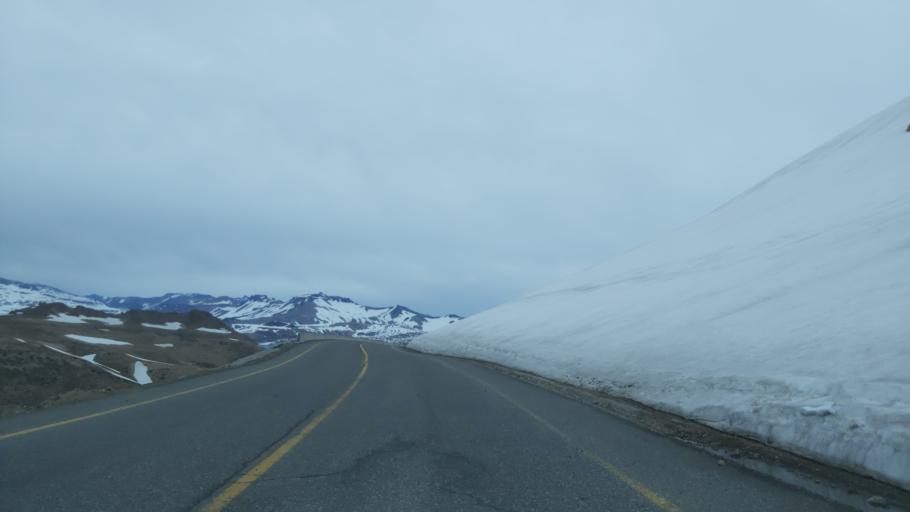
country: CL
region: Maule
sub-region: Provincia de Linares
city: Colbun
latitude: -36.0175
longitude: -70.4983
